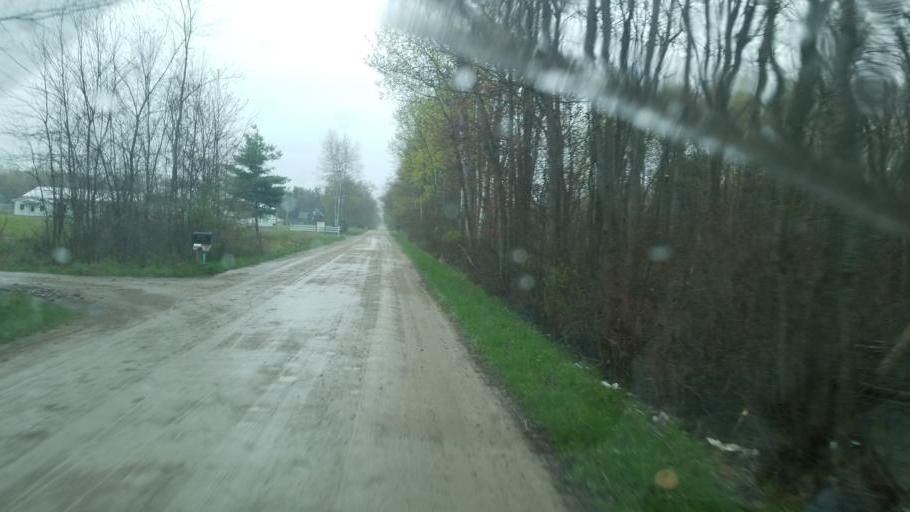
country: US
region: Michigan
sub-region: Mecosta County
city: Canadian Lakes
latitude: 43.5261
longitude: -85.3039
